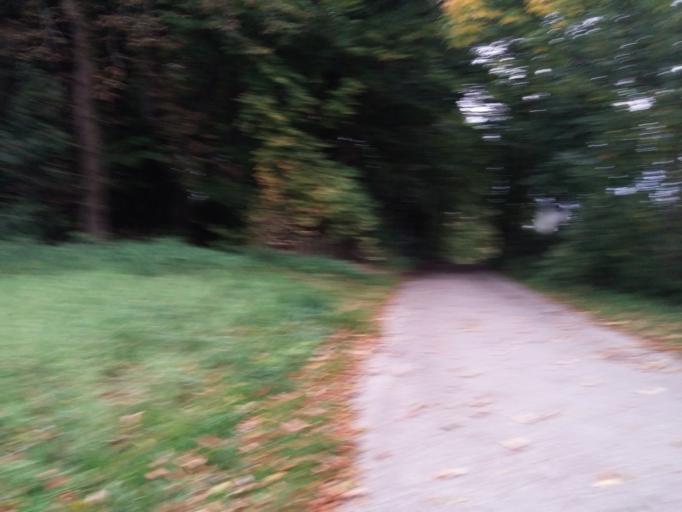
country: DE
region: Bavaria
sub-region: Upper Bavaria
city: Kirchseeon
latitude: 48.0738
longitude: 11.8917
